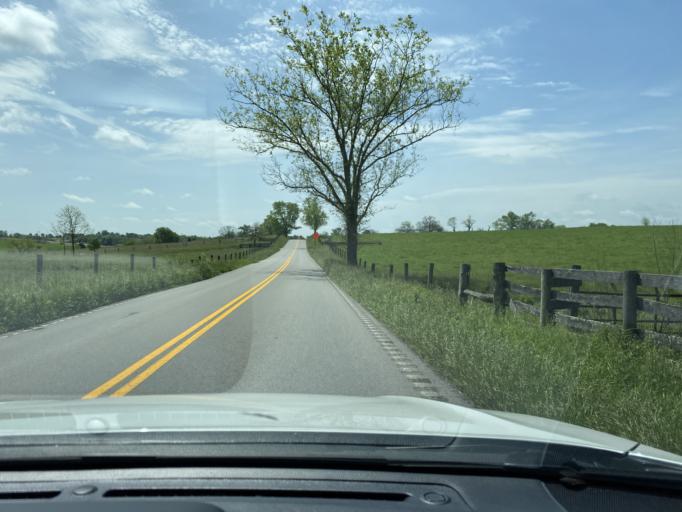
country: US
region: Kentucky
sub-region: Scott County
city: Georgetown
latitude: 38.2485
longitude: -84.5880
